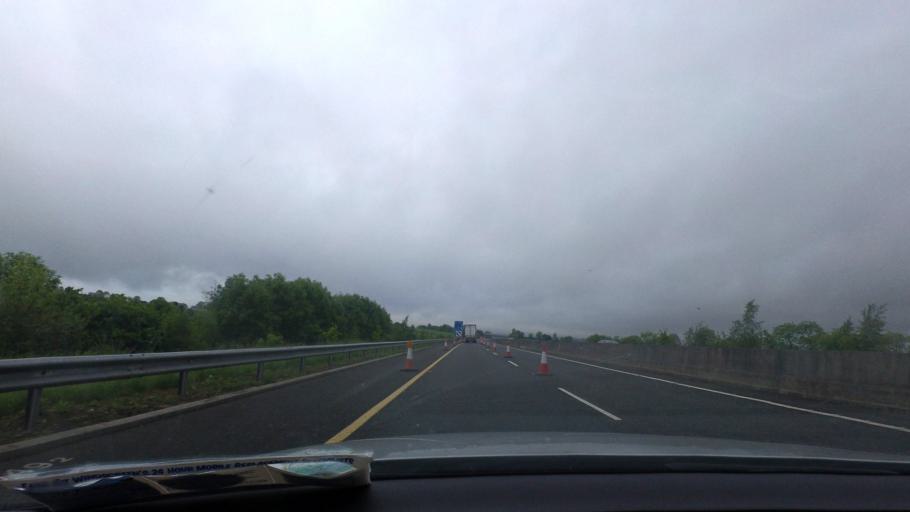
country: IE
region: Munster
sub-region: North Tipperary
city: Nenagh
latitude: 52.8444
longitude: -8.2184
